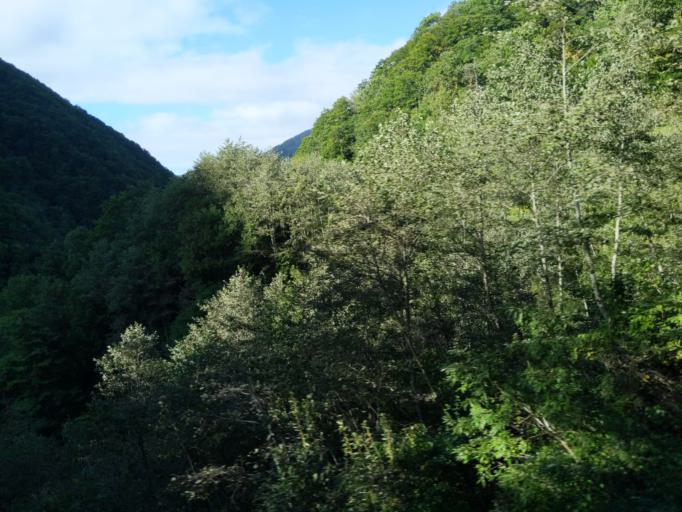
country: JP
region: Toyama
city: Kamiichi
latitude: 36.5155
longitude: 137.4493
